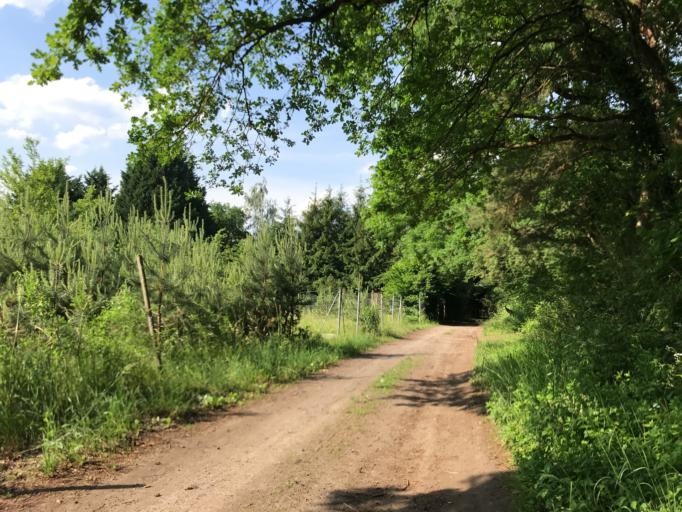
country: DE
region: Hesse
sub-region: Regierungsbezirk Darmstadt
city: Eltville
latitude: 50.0112
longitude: 8.1359
